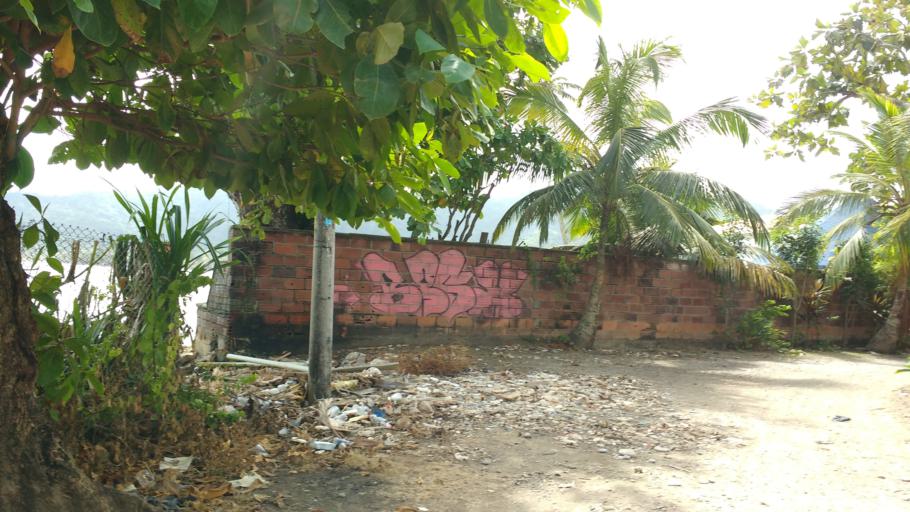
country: PA
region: Guna Yala
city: Puerto Obaldia
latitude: 8.6371
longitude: -77.3464
